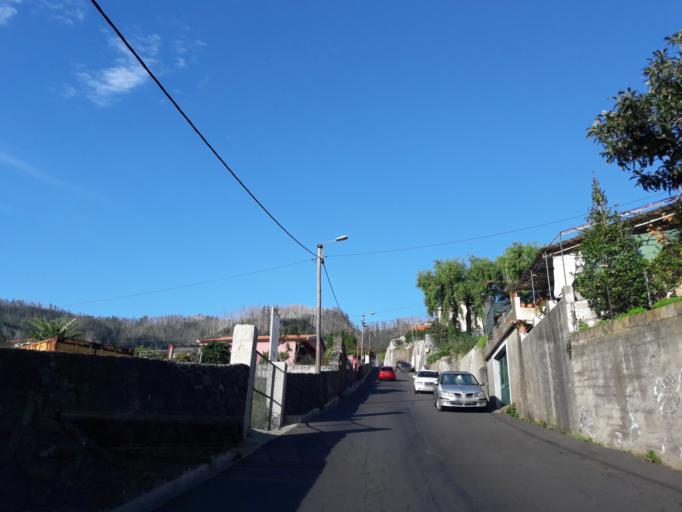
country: PT
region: Madeira
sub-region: Funchal
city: Nossa Senhora do Monte
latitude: 32.6729
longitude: -16.9209
